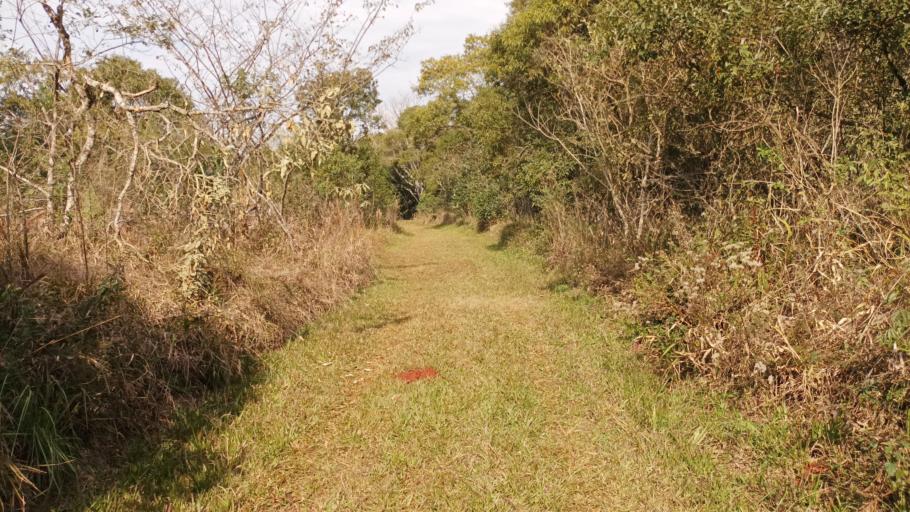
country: AR
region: Misiones
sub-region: Departamento de San Pedro
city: San Pedro
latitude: -26.6294
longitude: -54.1045
